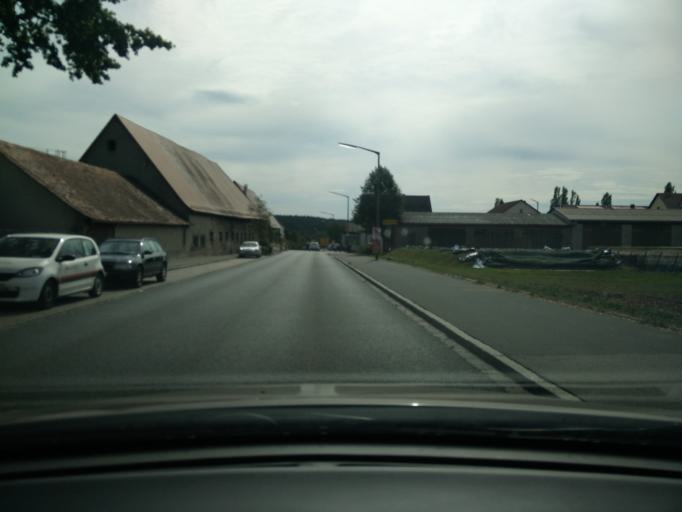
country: DE
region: Bavaria
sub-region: Regierungsbezirk Mittelfranken
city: Seukendorf
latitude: 49.4879
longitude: 10.8768
